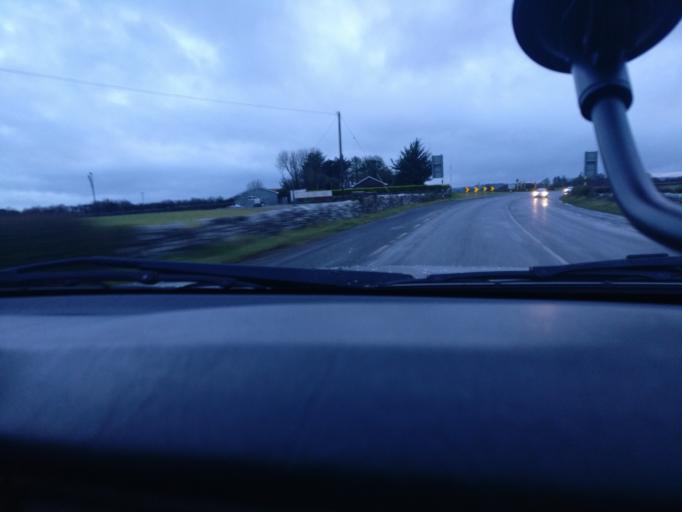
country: IE
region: Connaught
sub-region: County Galway
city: Loughrea
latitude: 53.2243
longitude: -8.4570
